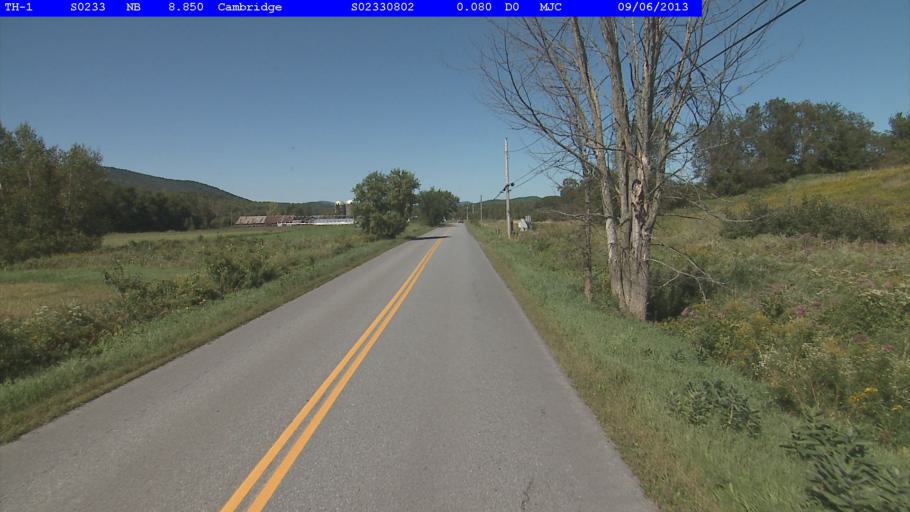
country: US
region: Vermont
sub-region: Chittenden County
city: Jericho
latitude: 44.5859
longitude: -72.8634
